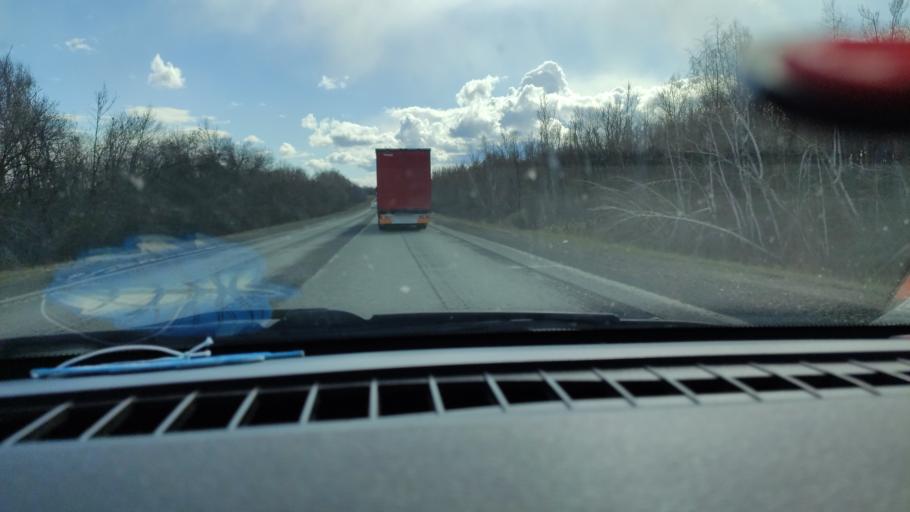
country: RU
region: Saratov
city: Dukhovnitskoye
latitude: 52.6267
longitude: 48.1806
